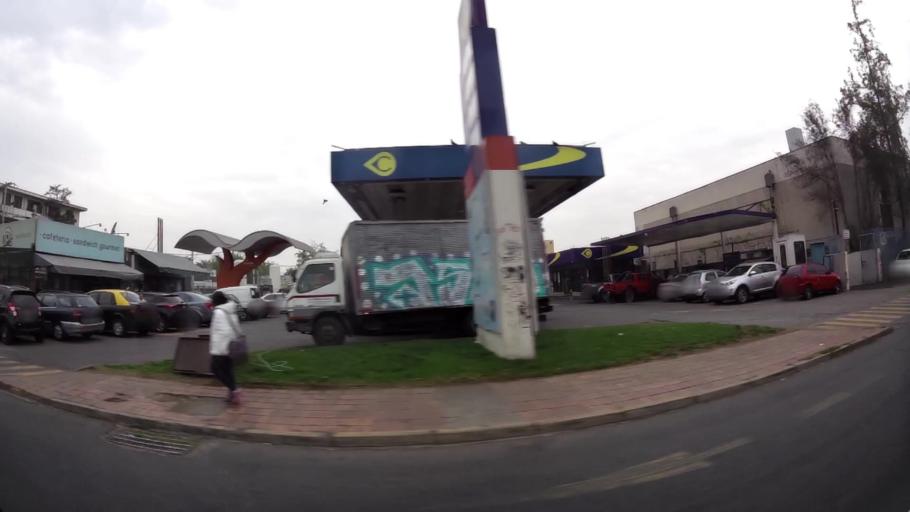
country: CL
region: Santiago Metropolitan
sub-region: Provincia de Santiago
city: Lo Prado
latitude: -33.4556
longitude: -70.6975
